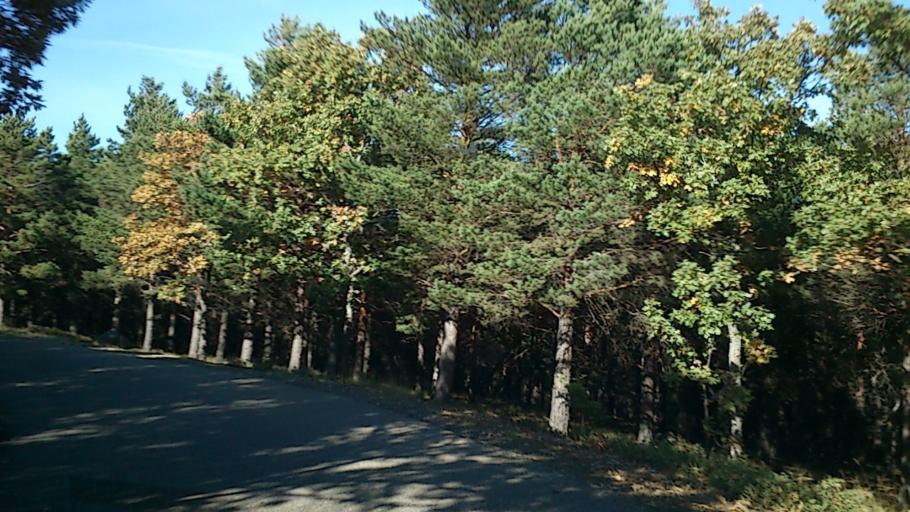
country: ES
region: Aragon
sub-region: Provincia de Zaragoza
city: Litago
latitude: 41.8046
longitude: -1.7888
